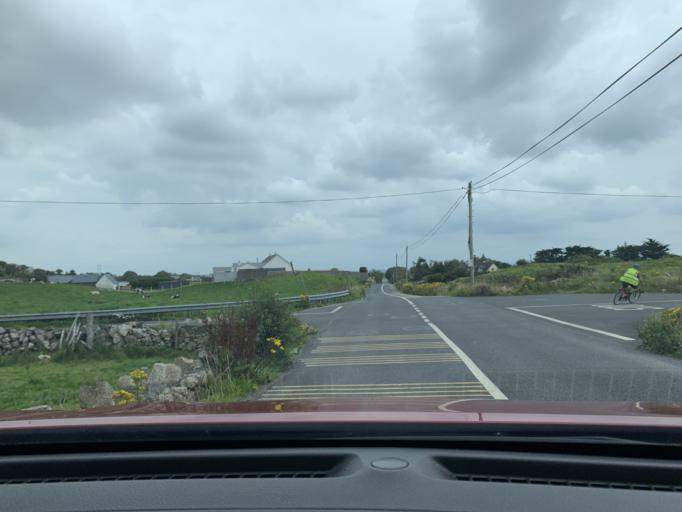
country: IE
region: Connaught
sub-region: County Galway
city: Bearna
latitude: 53.2791
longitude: -9.1078
